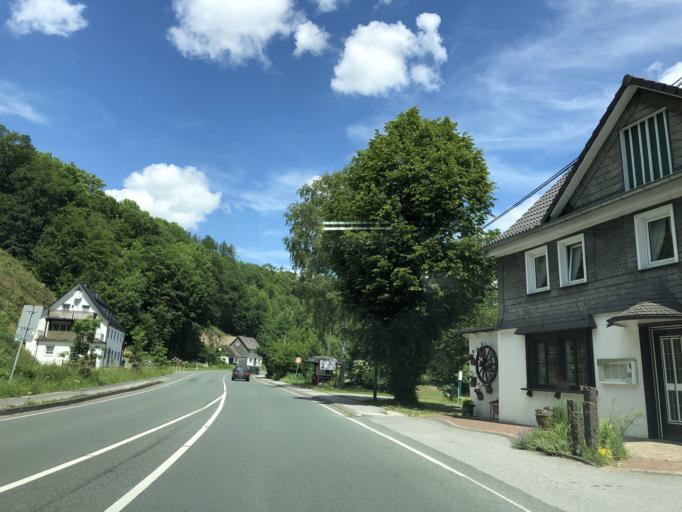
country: DE
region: North Rhine-Westphalia
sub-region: Regierungsbezirk Arnsberg
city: Schmallenberg
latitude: 51.1342
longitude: 8.2206
